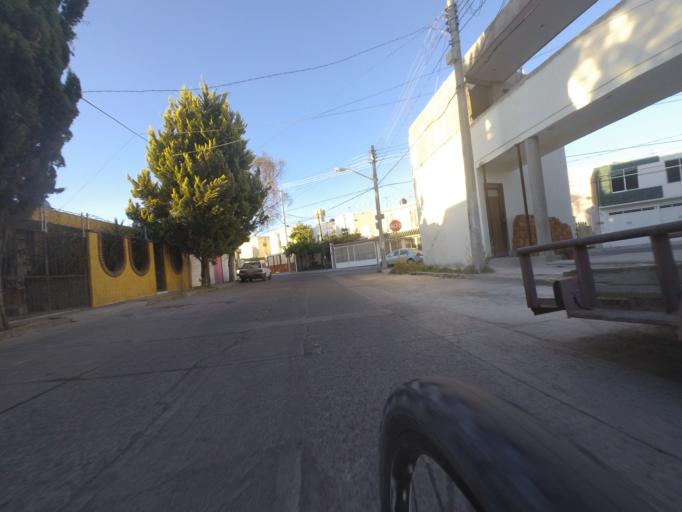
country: MX
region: Aguascalientes
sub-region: Aguascalientes
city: La Loma de los Negritos
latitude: 21.8551
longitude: -102.3397
